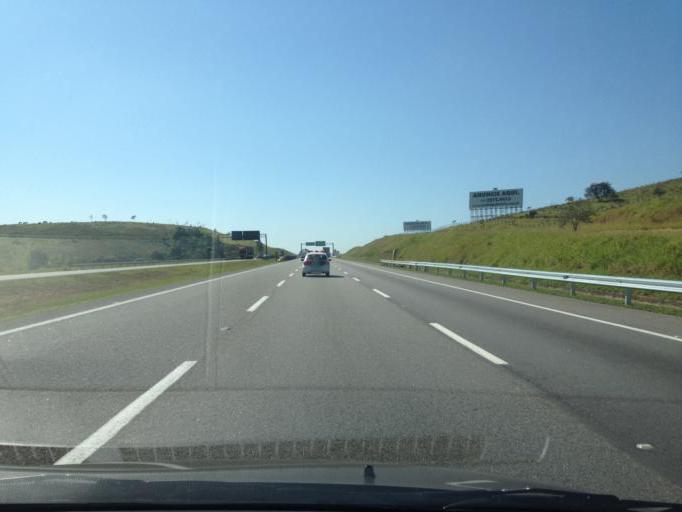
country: BR
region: Sao Paulo
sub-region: Guararema
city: Guararema
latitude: -23.3476
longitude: -46.0452
